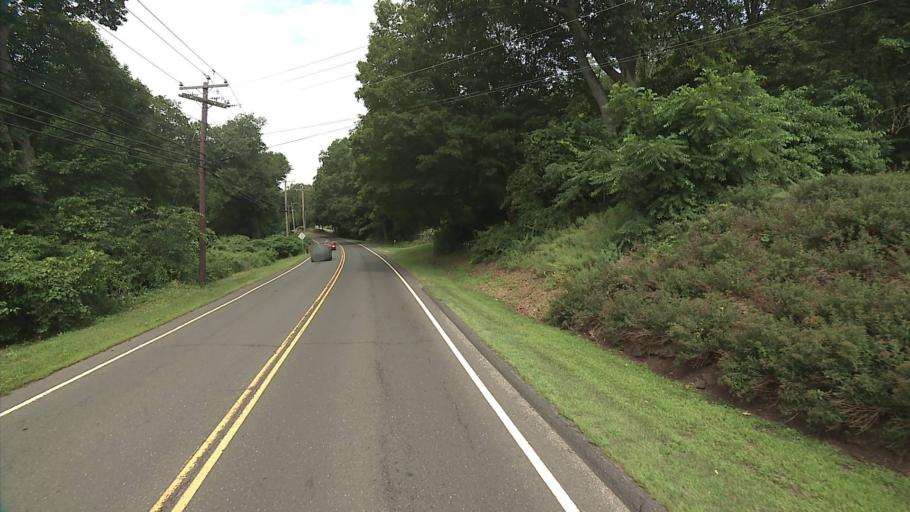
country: US
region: Connecticut
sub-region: New Haven County
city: Oxford
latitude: 41.4386
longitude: -73.1222
